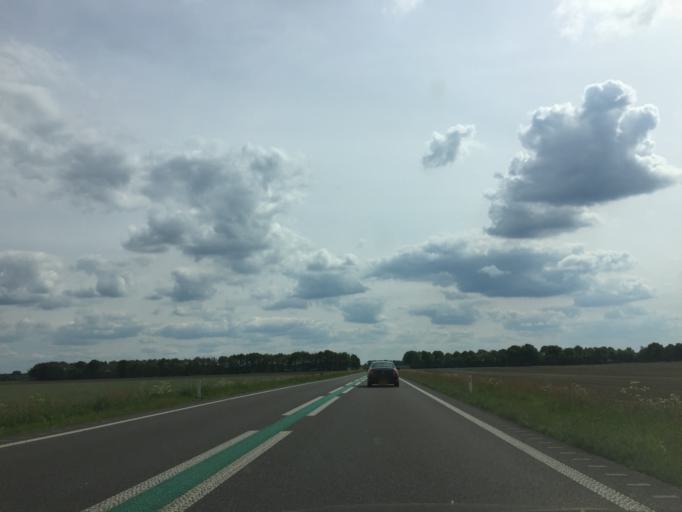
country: NL
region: Drenthe
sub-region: Gemeente Borger-Odoorn
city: Borger
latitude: 52.9446
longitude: 6.7843
